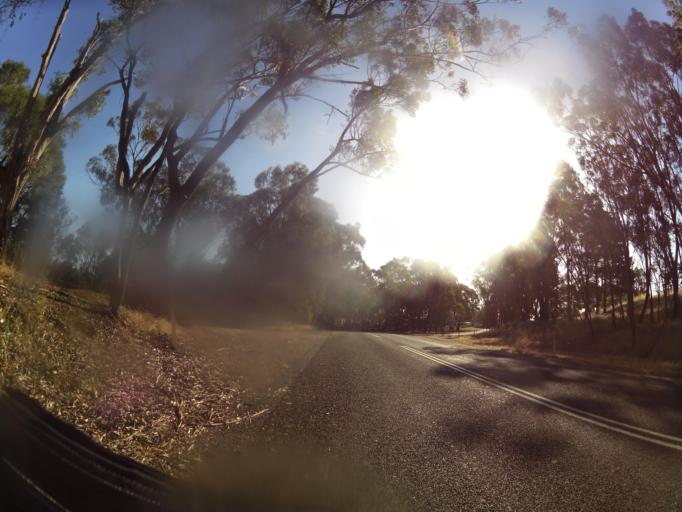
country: AU
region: Victoria
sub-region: Murrindindi
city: Kinglake West
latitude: -37.0217
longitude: 145.1048
